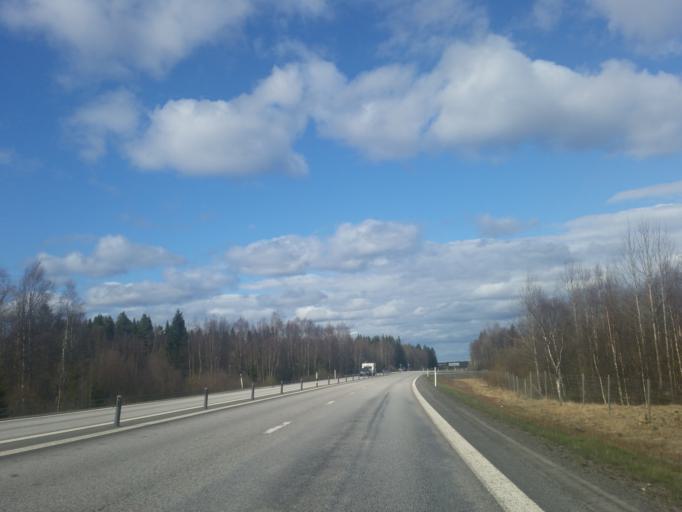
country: SE
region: Vaesterbotten
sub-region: Robertsfors Kommun
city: Robertsfors
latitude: 64.0656
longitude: 20.8500
